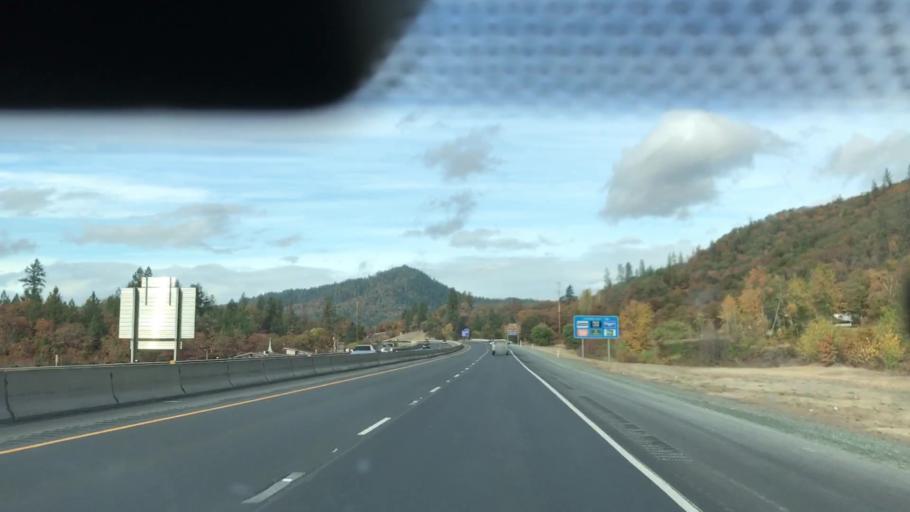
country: US
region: Oregon
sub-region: Josephine County
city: Grants Pass
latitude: 42.4559
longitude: -123.3099
